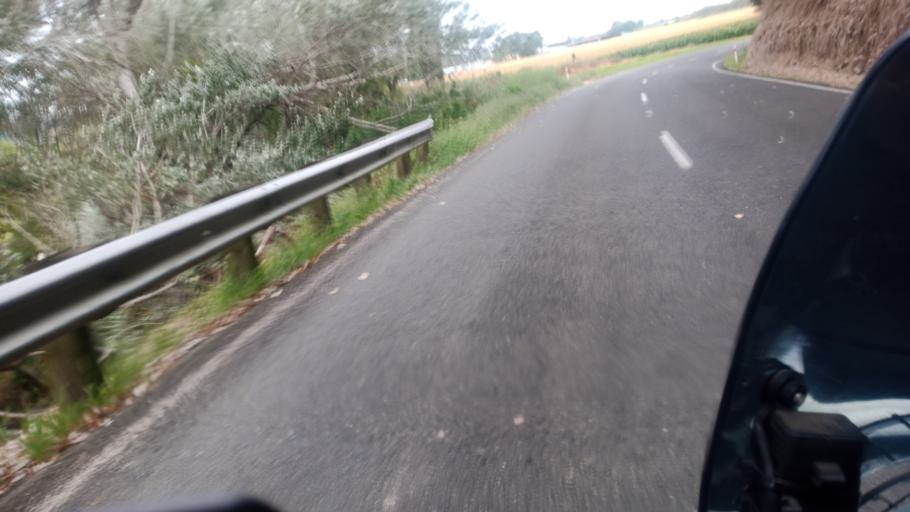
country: NZ
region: Gisborne
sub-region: Gisborne District
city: Gisborne
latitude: -38.5688
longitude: 177.9071
